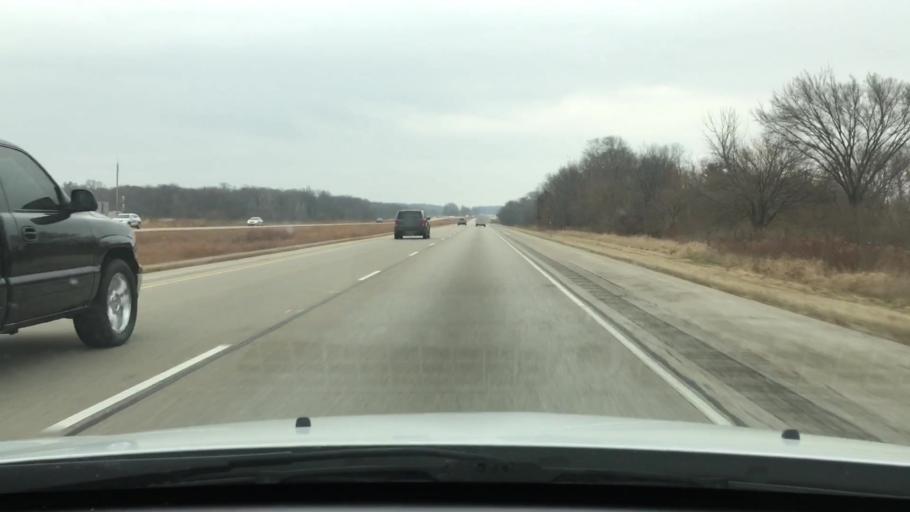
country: US
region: Illinois
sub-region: Logan County
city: Atlanta
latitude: 40.3368
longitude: -89.1424
